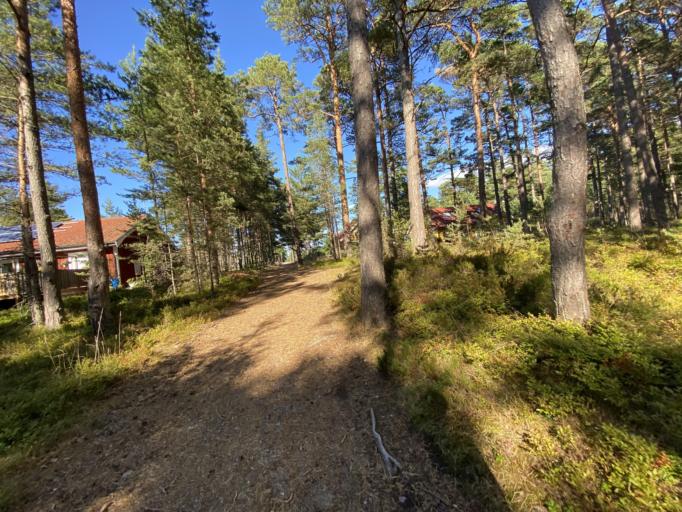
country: SE
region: Stockholm
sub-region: Varmdo Kommun
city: Holo
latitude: 59.2853
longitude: 18.9058
